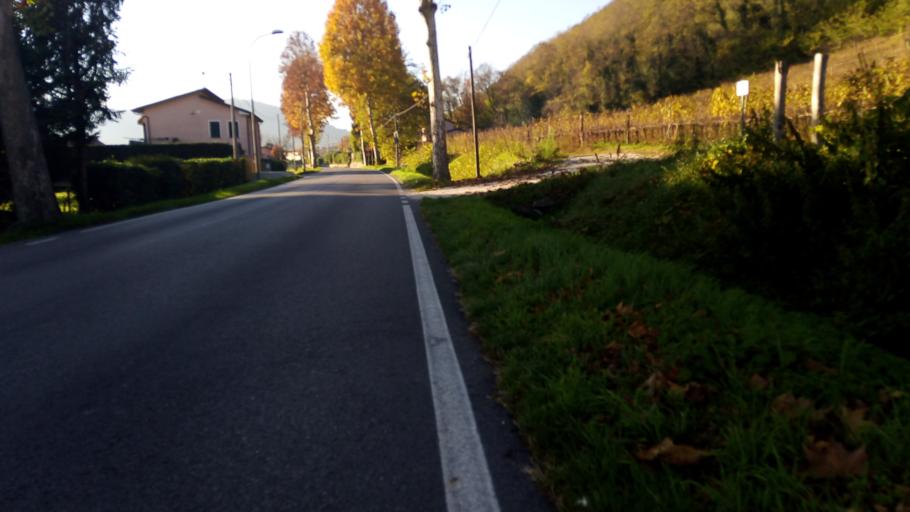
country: IT
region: Veneto
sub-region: Provincia di Padova
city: San Biagio
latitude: 45.3664
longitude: 11.7548
